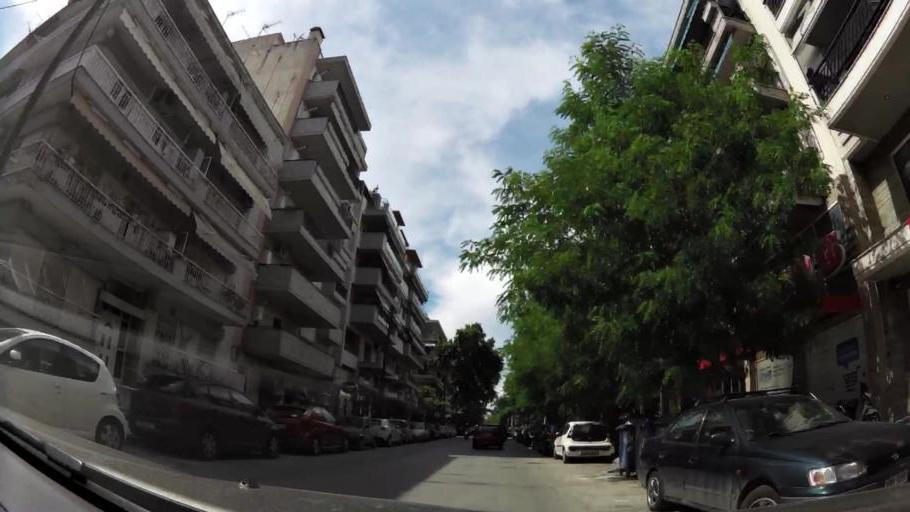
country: GR
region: Central Macedonia
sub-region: Nomos Thessalonikis
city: Triandria
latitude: 40.6066
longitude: 22.9708
